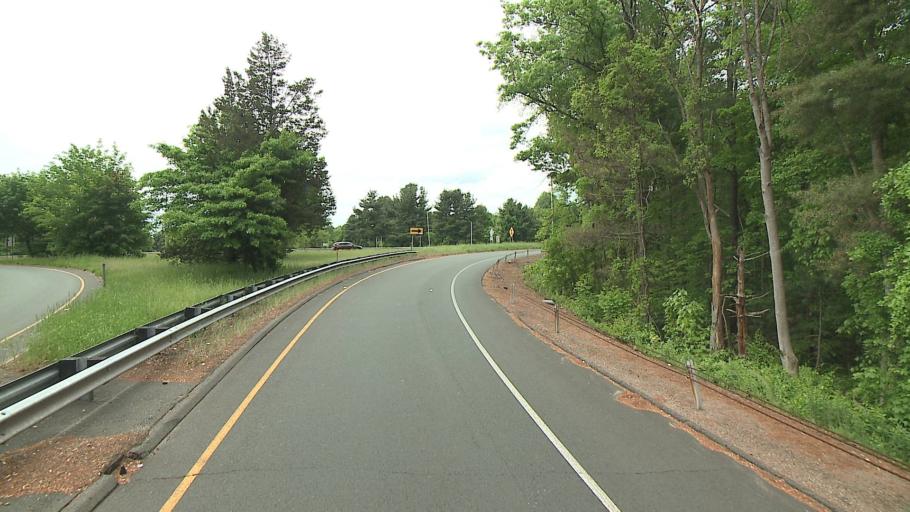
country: US
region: Connecticut
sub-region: Hartford County
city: Thompsonville
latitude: 41.9910
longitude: -72.5893
